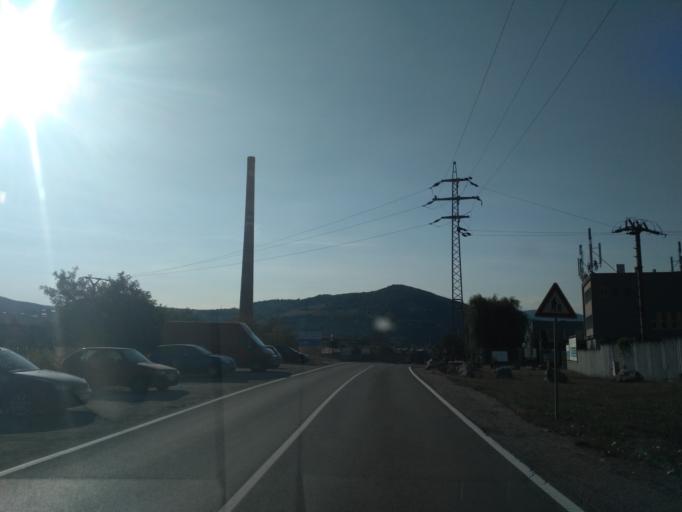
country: SK
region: Kosicky
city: Kosice
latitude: 48.7487
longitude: 21.2659
